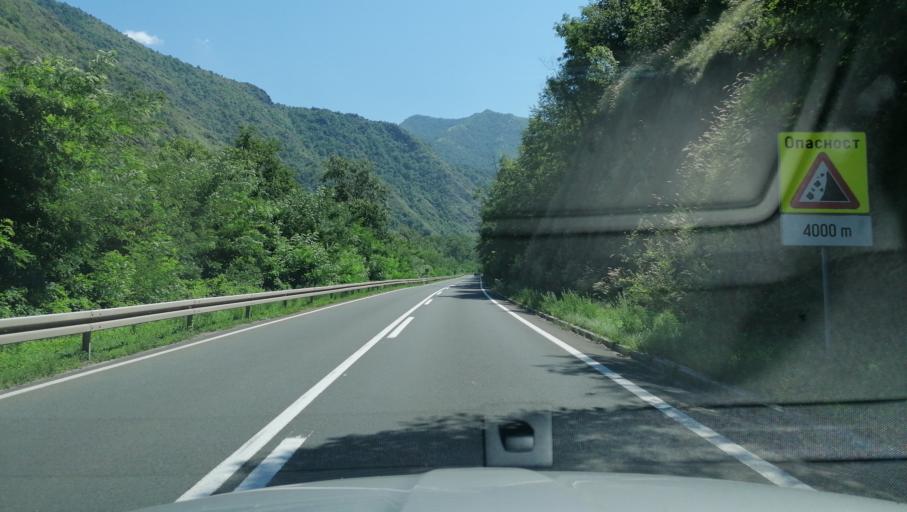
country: RS
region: Central Serbia
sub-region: Raski Okrug
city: Kraljevo
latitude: 43.6237
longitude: 20.5476
